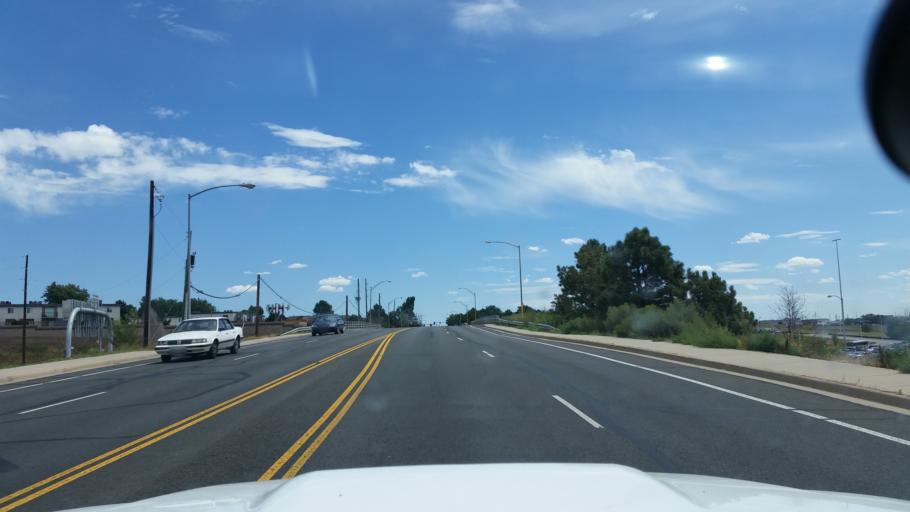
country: US
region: Colorado
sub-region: Adams County
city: Federal Heights
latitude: 39.8563
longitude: -104.9887
